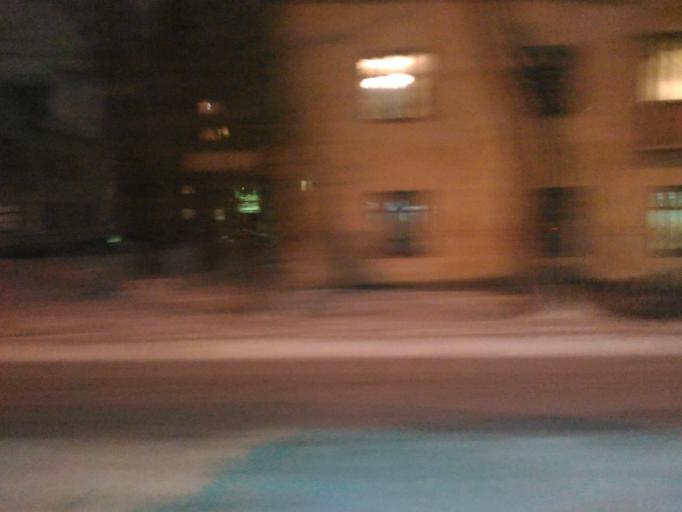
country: RU
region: Ulyanovsk
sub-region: Ulyanovskiy Rayon
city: Ulyanovsk
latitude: 54.3247
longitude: 48.3803
